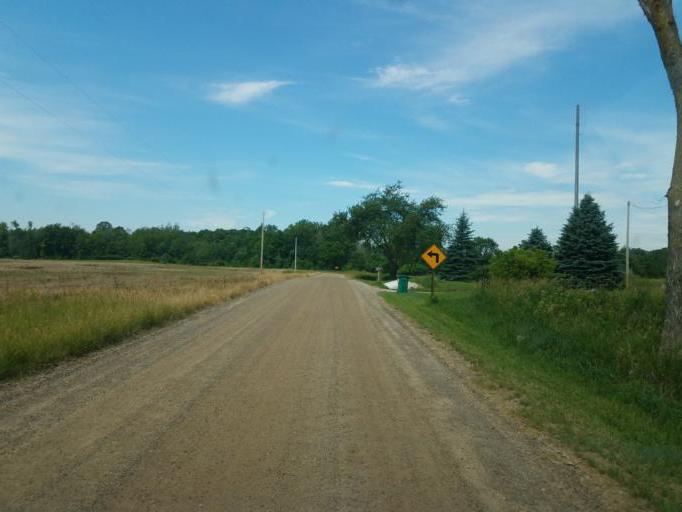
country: US
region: Michigan
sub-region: Eaton County
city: Charlotte
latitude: 42.5895
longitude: -84.8197
